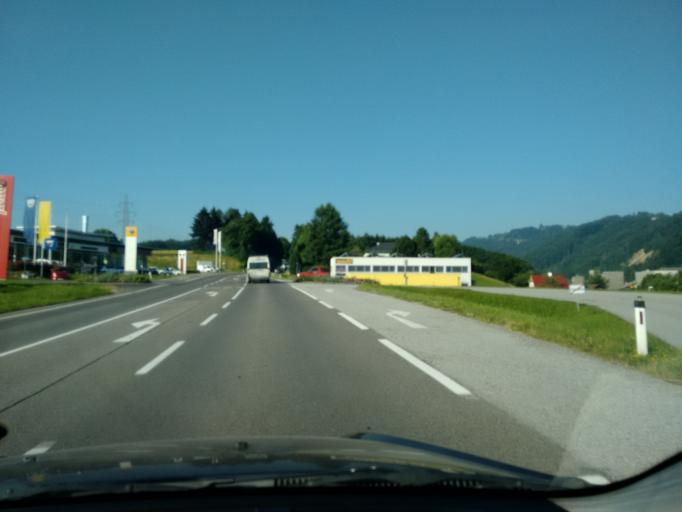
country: AT
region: Upper Austria
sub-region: Politischer Bezirk Gmunden
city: Gmunden
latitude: 47.9231
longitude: 13.7835
